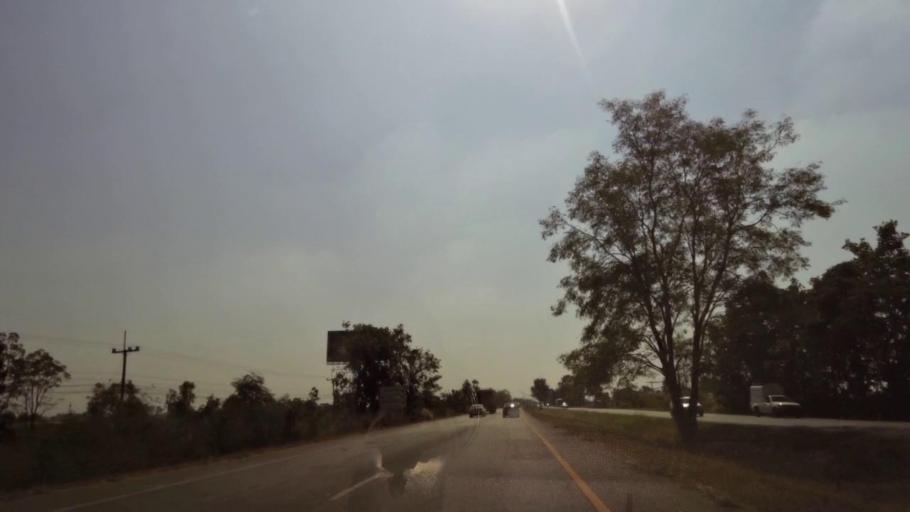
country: TH
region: Phichit
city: Wachira Barami
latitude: 16.4660
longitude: 100.1473
